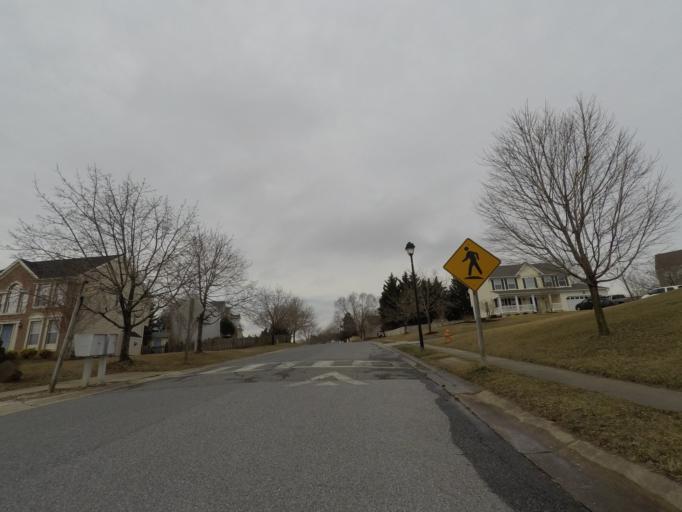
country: US
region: Maryland
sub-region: Howard County
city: Ilchester
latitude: 39.2206
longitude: -76.7766
